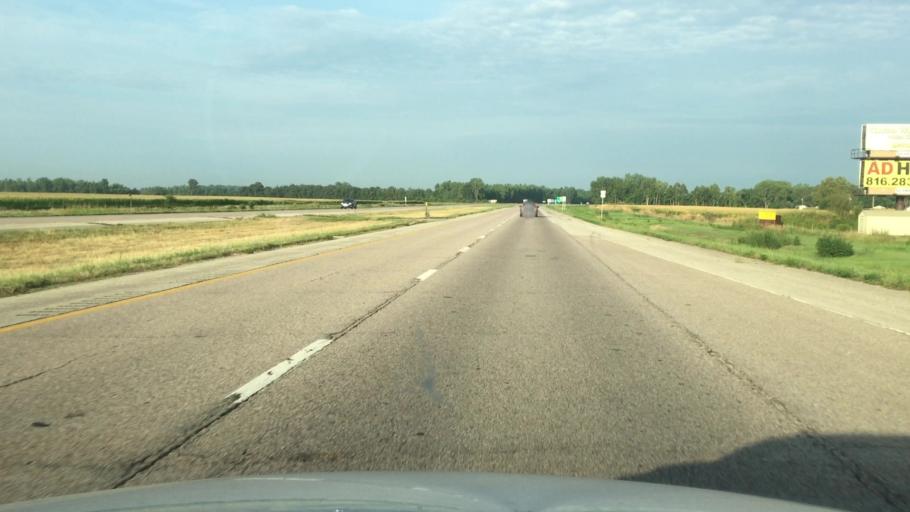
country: US
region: Kansas
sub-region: Doniphan County
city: Elwood
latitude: 39.7482
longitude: -94.8743
